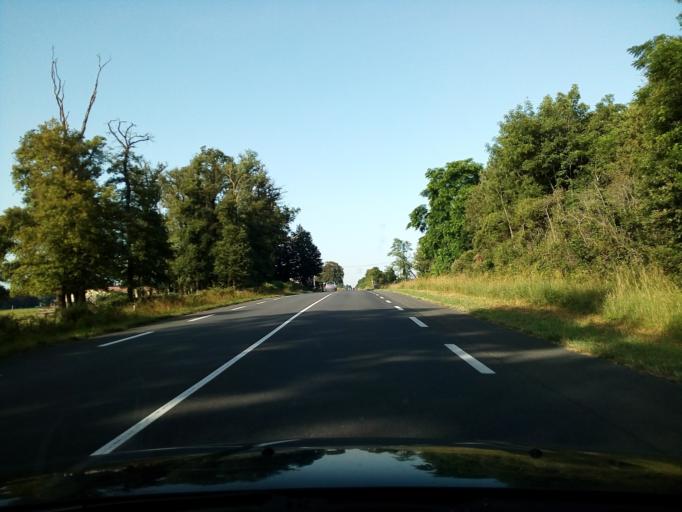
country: FR
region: Poitou-Charentes
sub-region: Departement de la Charente
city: Loubert
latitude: 45.9818
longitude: 0.6016
